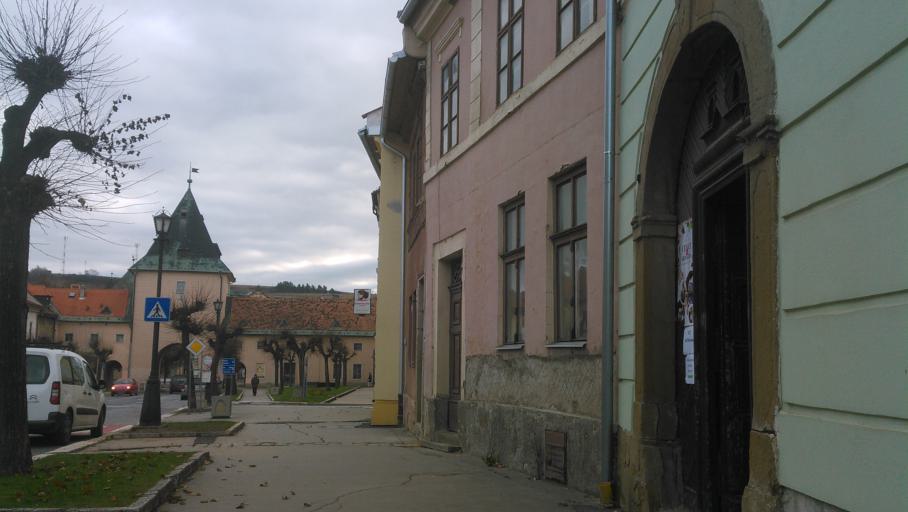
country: SK
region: Presovsky
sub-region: Okres Presov
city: Levoca
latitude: 49.0273
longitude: 20.5920
